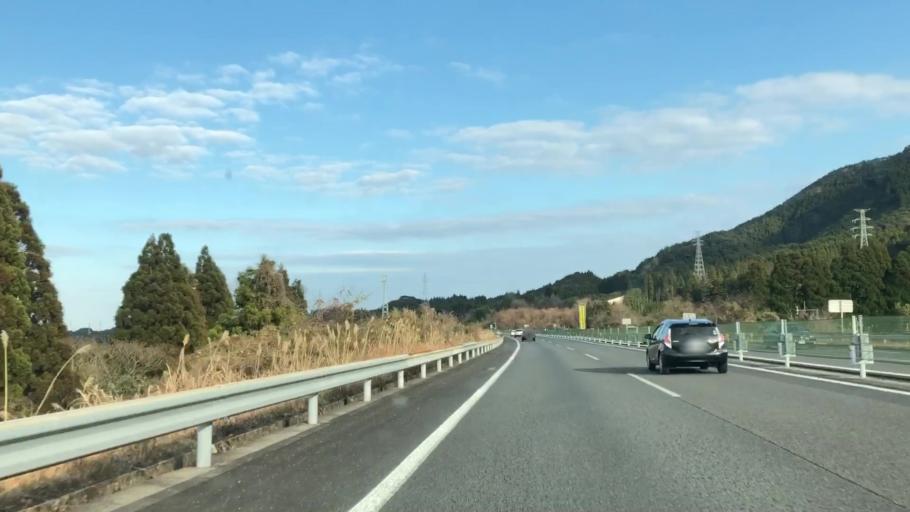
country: JP
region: Miyazaki
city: Miyazaki-shi
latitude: 31.8336
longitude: 131.3348
